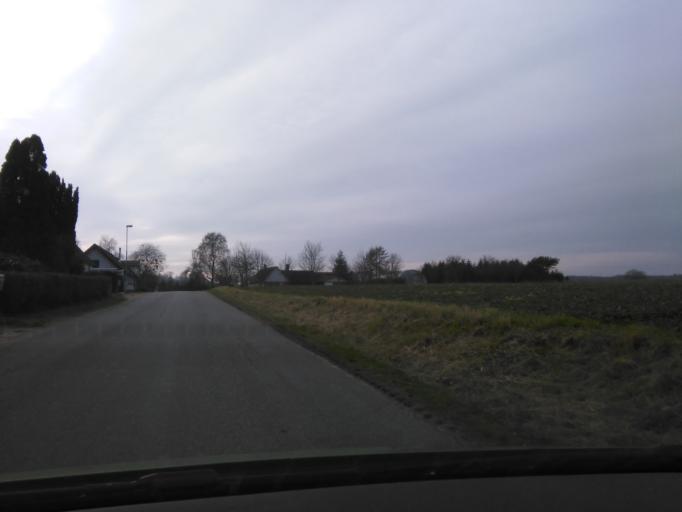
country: DK
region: Central Jutland
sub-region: Odder Kommune
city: Odder
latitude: 55.9268
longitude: 10.1320
